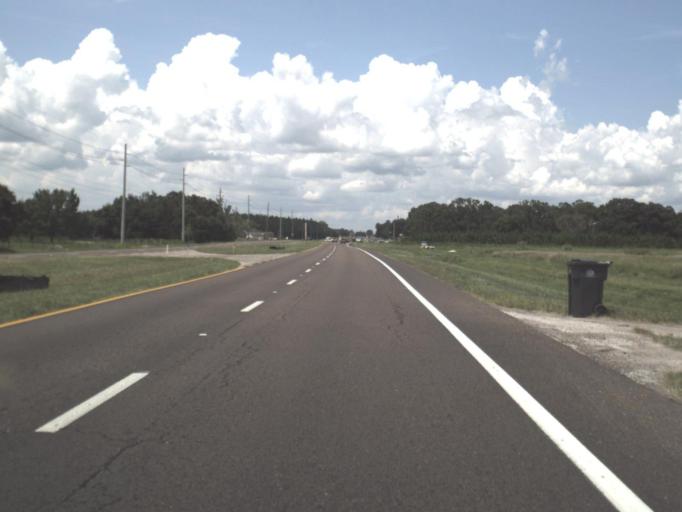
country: US
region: Florida
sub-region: Hillsborough County
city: Plant City
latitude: 27.9614
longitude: -82.1211
